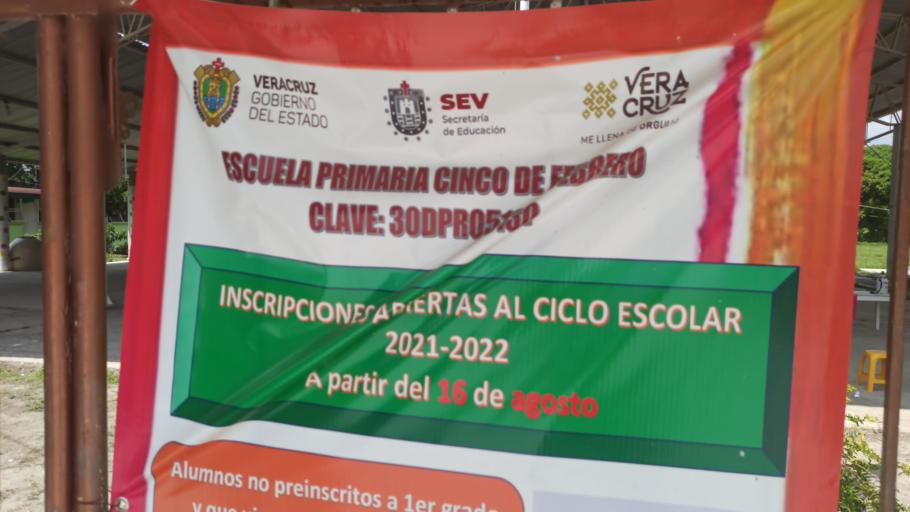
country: MX
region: Puebla
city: San Jose Acateno
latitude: 20.1724
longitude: -97.1128
